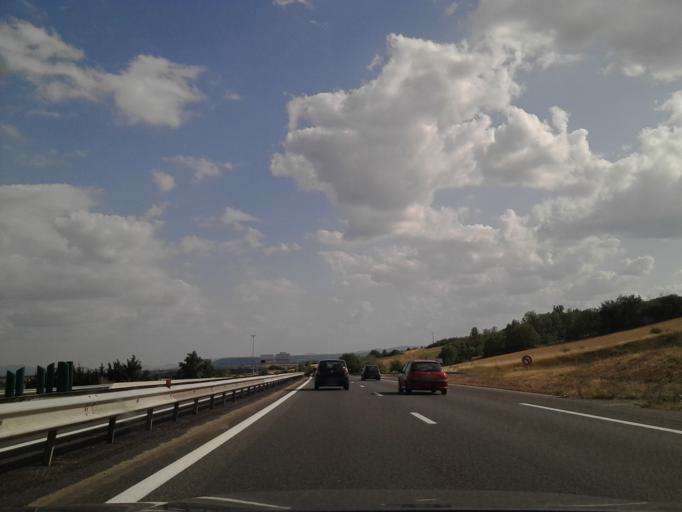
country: FR
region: Auvergne
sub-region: Departement du Puy-de-Dome
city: Combronde
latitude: 45.9712
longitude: 3.1002
